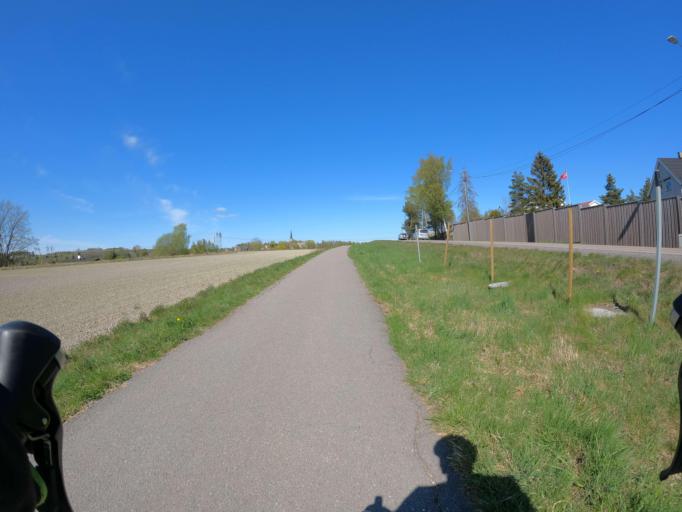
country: NO
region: Akershus
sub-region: Skedsmo
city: Lillestrom
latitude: 59.9879
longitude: 11.0310
